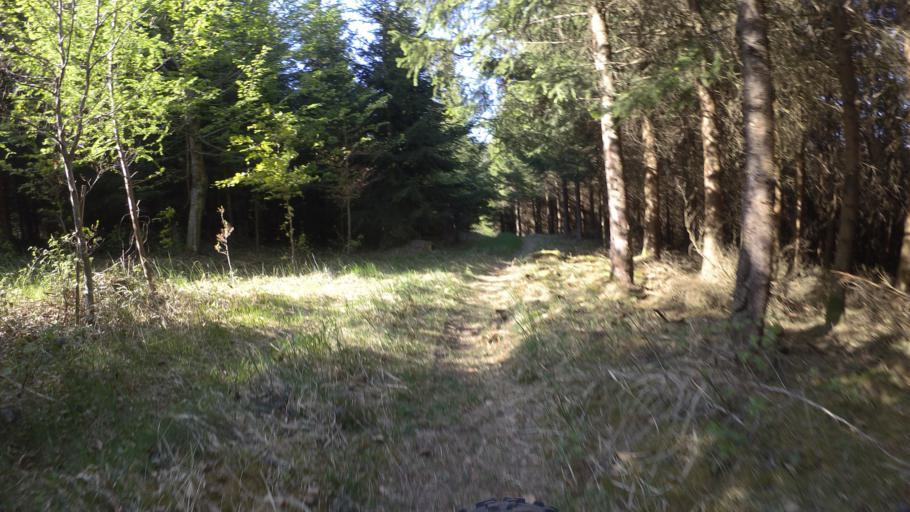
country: DE
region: Bavaria
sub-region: Upper Bavaria
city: Chieming
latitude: 47.9432
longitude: 12.5385
